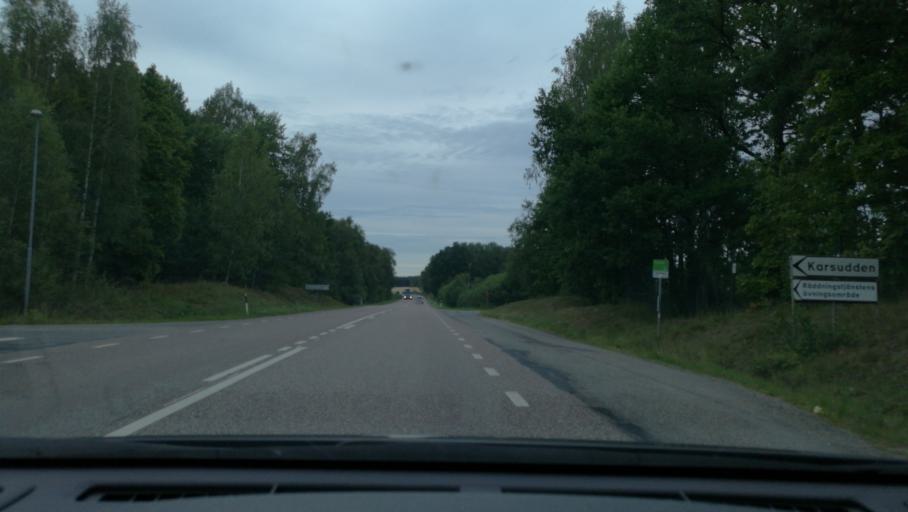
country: SE
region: Soedermanland
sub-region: Katrineholms Kommun
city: Katrineholm
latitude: 59.0127
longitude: 16.2135
